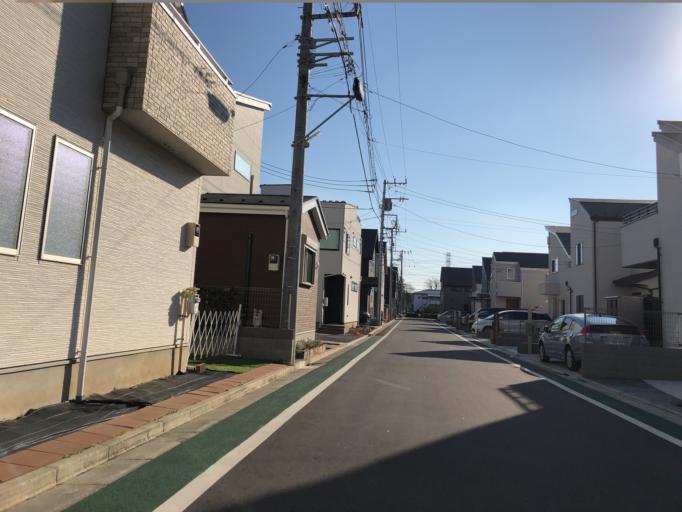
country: JP
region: Tokyo
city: Mitaka-shi
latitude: 35.6858
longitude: 139.5441
